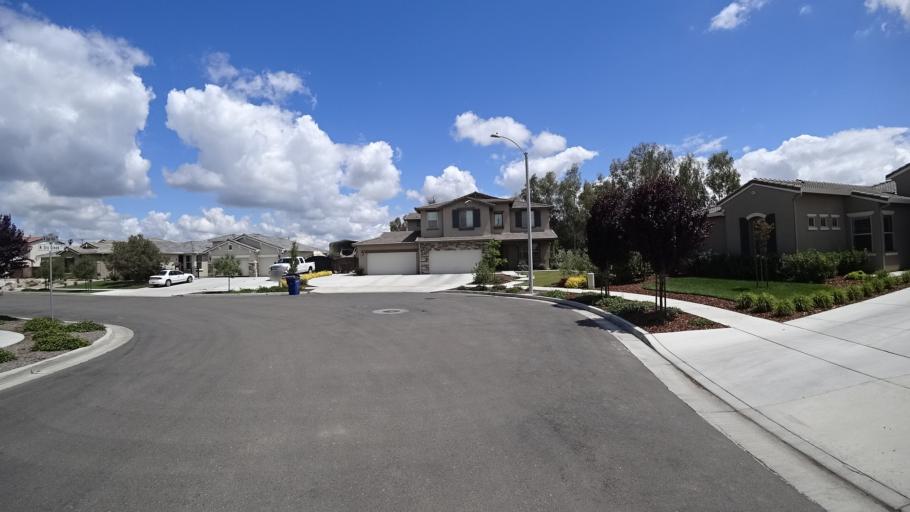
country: US
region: California
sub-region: Kings County
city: Lucerne
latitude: 36.3701
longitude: -119.6582
